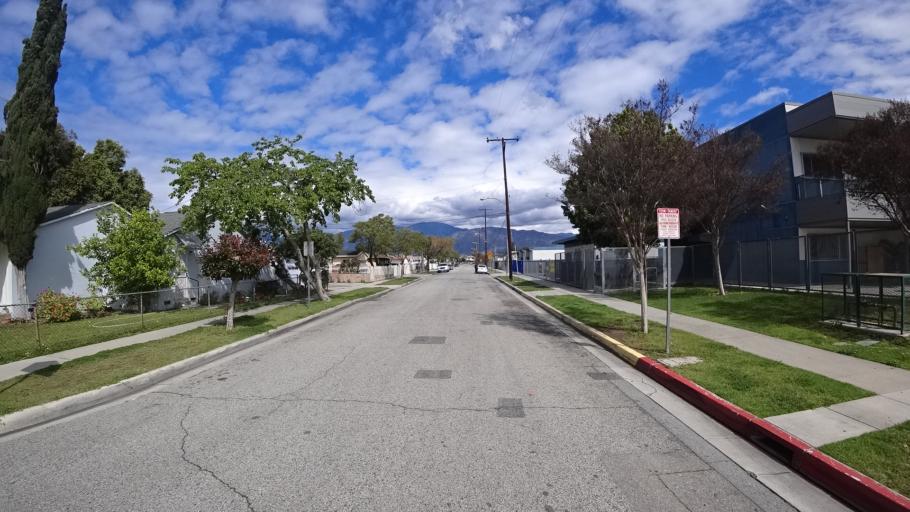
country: US
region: California
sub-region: Los Angeles County
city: Baldwin Park
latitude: 34.0956
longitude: -117.9577
